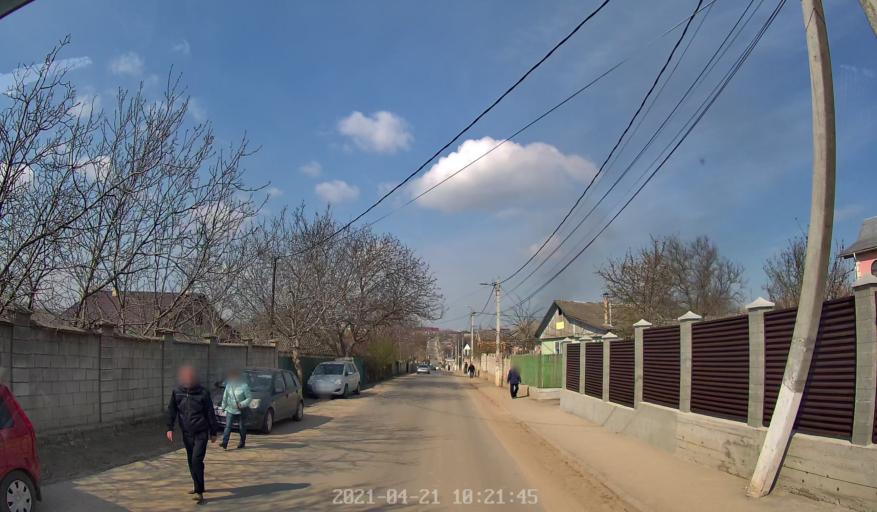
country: MD
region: Chisinau
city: Singera
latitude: 46.9843
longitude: 28.9415
